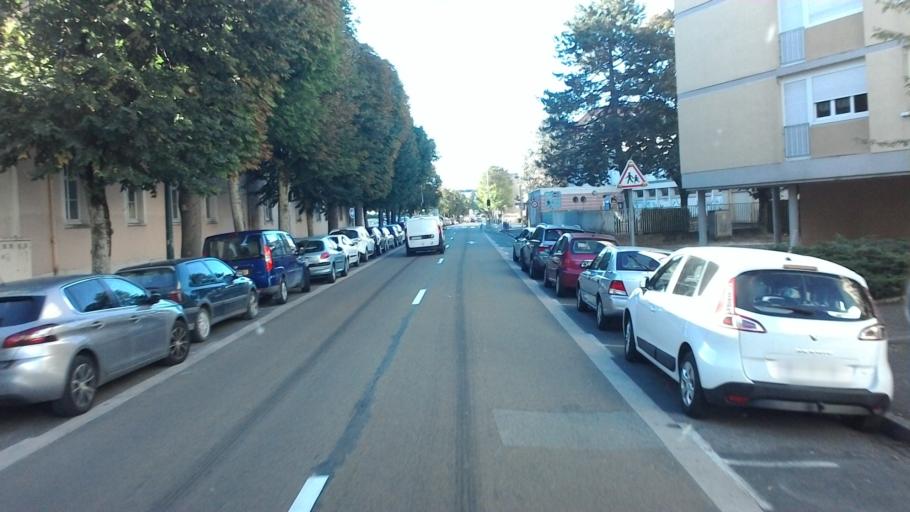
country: FR
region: Champagne-Ardenne
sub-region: Departement de la Haute-Marne
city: Chaumont
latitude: 48.1134
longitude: 5.1429
